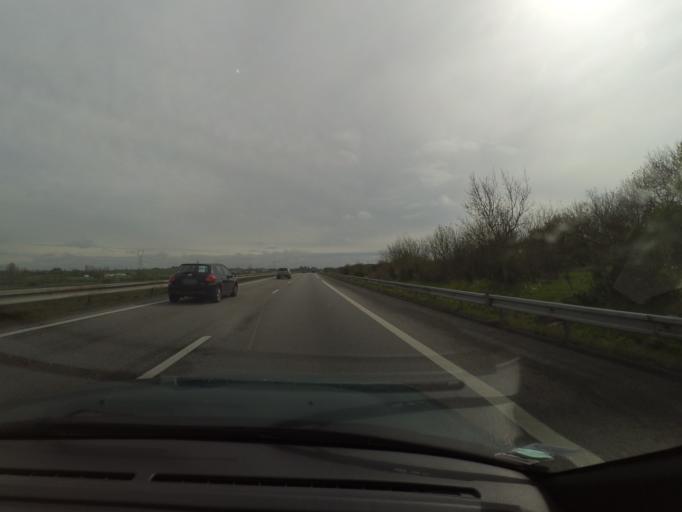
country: FR
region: Pays de la Loire
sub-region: Departement de la Loire-Atlantique
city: Saint-Herblon
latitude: 47.4200
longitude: -1.1098
